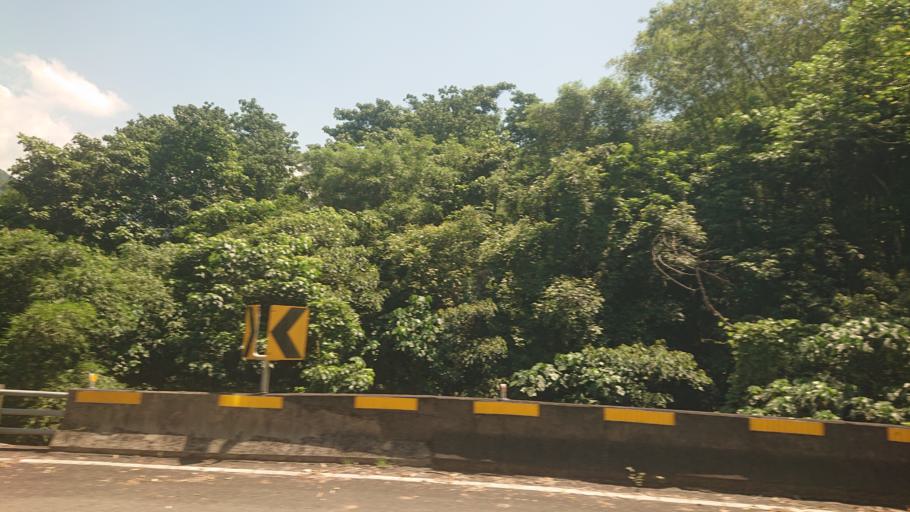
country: TW
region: Taiwan
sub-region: Nantou
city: Puli
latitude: 24.0571
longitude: 120.9357
